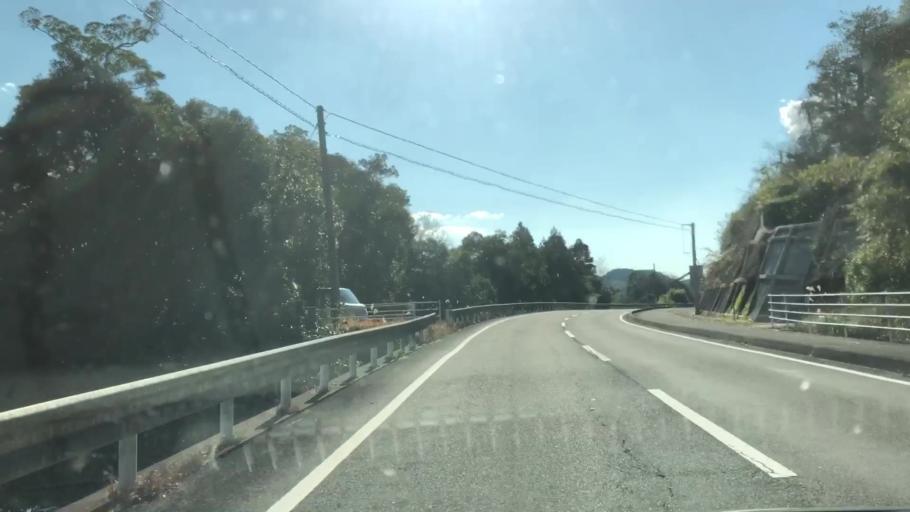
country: JP
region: Kagoshima
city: Satsumasendai
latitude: 31.8637
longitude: 130.4188
